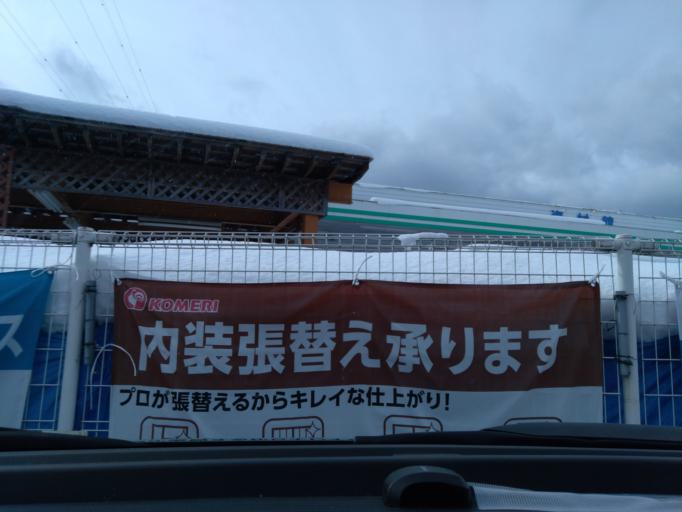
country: JP
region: Akita
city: Kakunodatemachi
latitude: 39.6944
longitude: 140.7211
